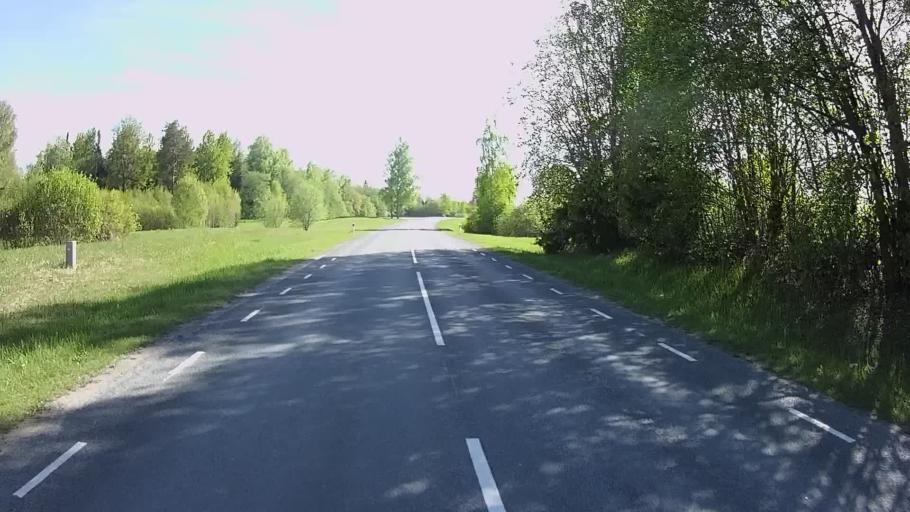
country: EE
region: Vorumaa
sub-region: Antsla vald
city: Vana-Antsla
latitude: 57.9601
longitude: 26.4528
